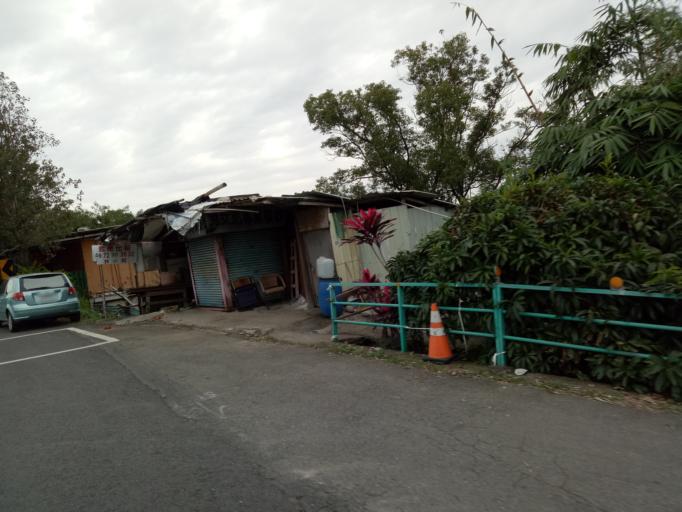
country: TW
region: Taiwan
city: Daxi
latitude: 24.8796
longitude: 121.2501
